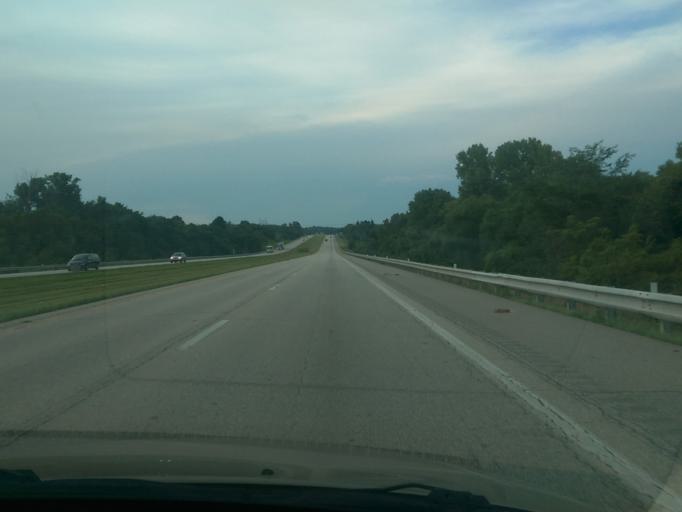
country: US
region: Missouri
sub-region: Andrew County
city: Country Club Village
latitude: 39.8351
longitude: -94.8051
